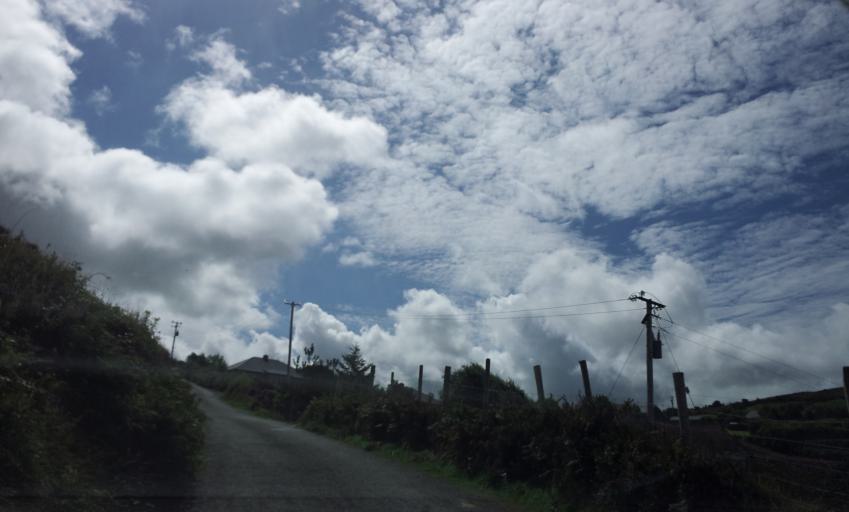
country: IE
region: Munster
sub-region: Ciarrai
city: Killorglin
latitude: 52.0475
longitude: -9.9875
